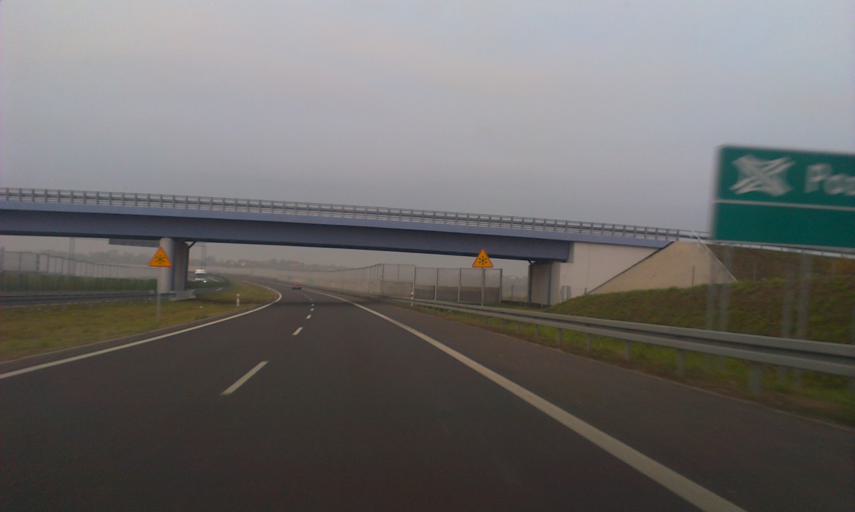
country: PL
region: Greater Poland Voivodeship
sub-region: Powiat poznanski
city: Rokietnica
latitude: 52.5169
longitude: 16.7954
